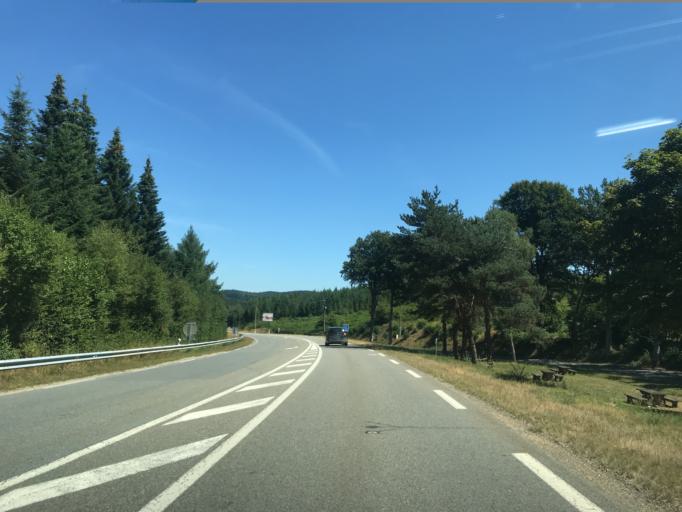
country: FR
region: Limousin
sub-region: Departement de la Correze
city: Meymac
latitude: 45.4589
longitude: 2.1287
